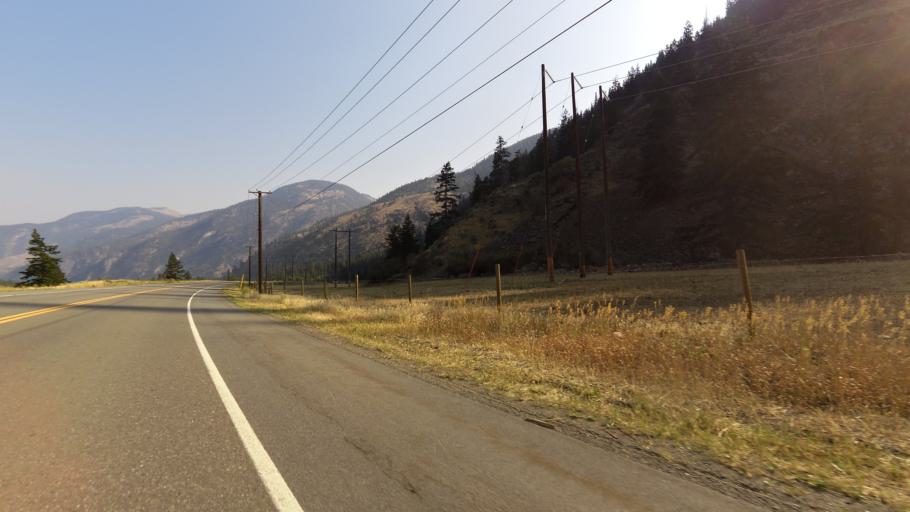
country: CA
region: British Columbia
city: Summerland
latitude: 49.2859
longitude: -120.0287
